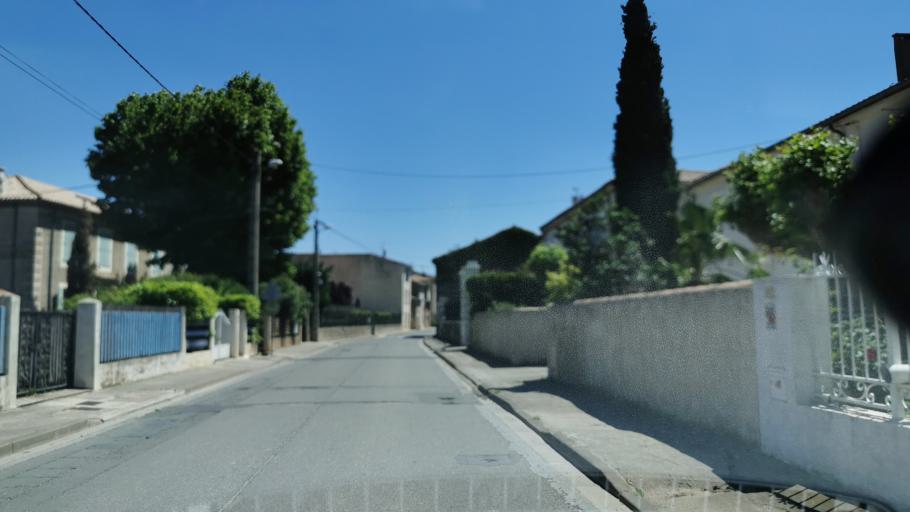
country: FR
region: Languedoc-Roussillon
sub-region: Departement de l'Aude
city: Saint-Marcel-sur-Aude
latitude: 43.2570
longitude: 2.9434
